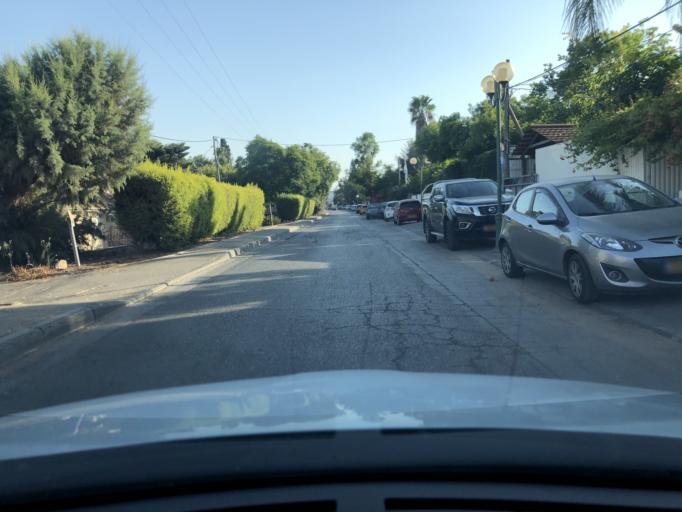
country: IL
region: Central District
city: Hod HaSharon
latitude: 32.1387
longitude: 34.9031
